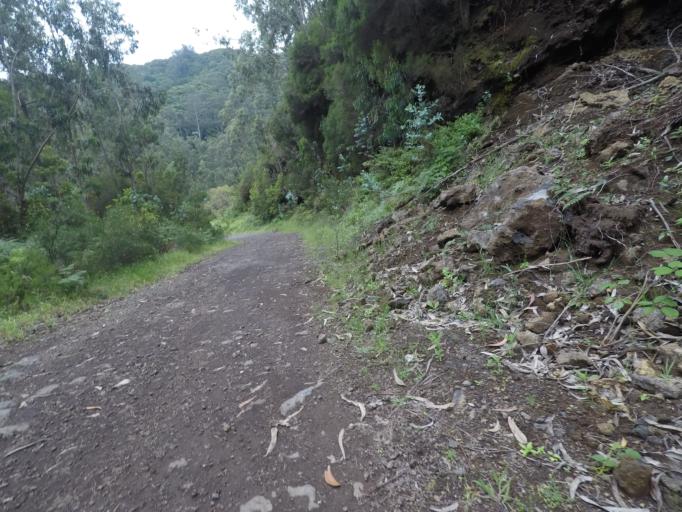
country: PT
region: Madeira
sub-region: Sao Vicente
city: Sao Vicente
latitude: 32.7740
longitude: -17.0483
